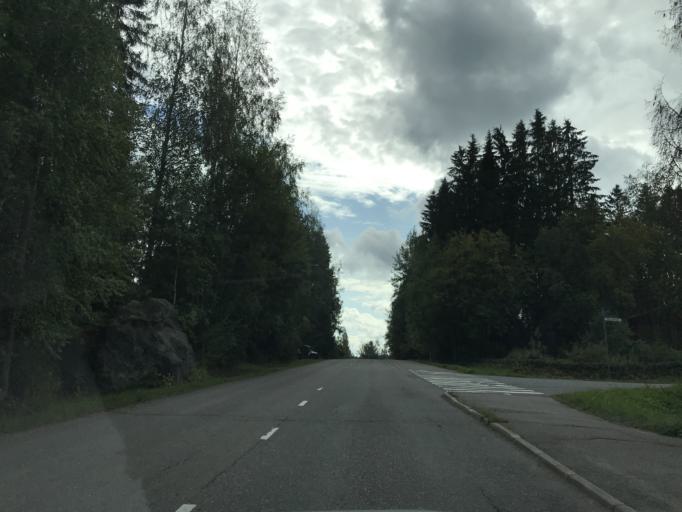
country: FI
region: Paijanne Tavastia
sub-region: Lahti
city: Orimattila
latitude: 60.8137
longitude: 25.7249
